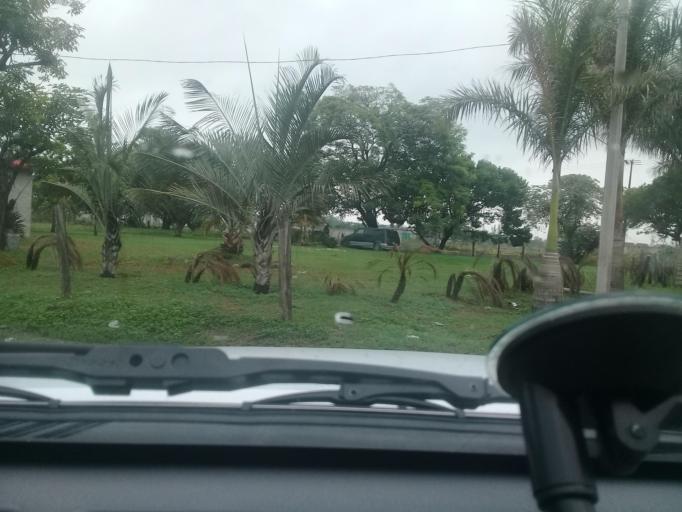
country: MX
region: Veracruz
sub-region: La Antigua
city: Nicolas Blanco (San Pancho)
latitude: 19.3395
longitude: -96.3619
